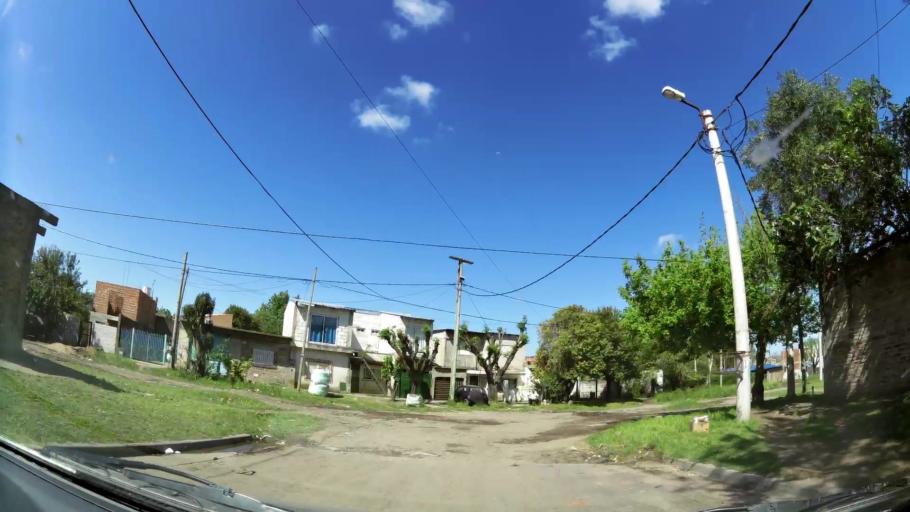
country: AR
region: Buenos Aires
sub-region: Partido de Quilmes
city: Quilmes
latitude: -34.8002
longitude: -58.2685
